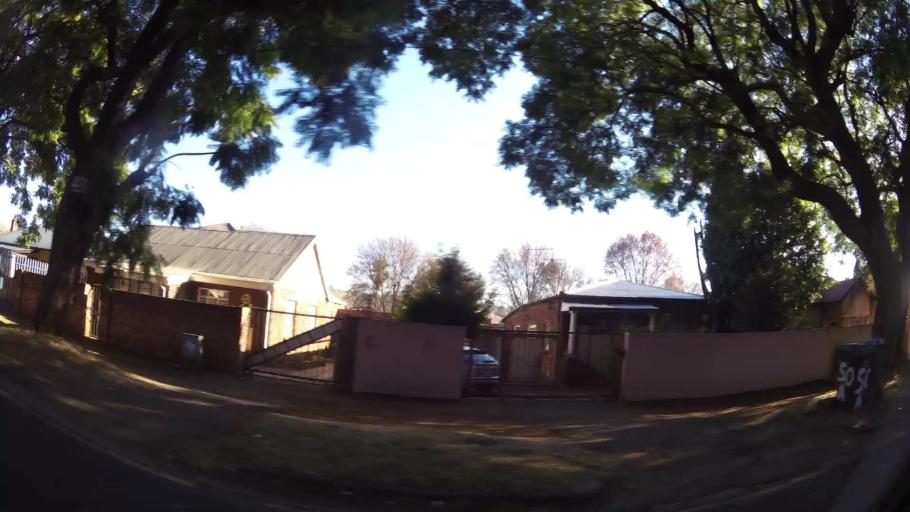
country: ZA
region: Gauteng
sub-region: City of Johannesburg Metropolitan Municipality
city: Johannesburg
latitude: -26.1893
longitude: 28.0902
